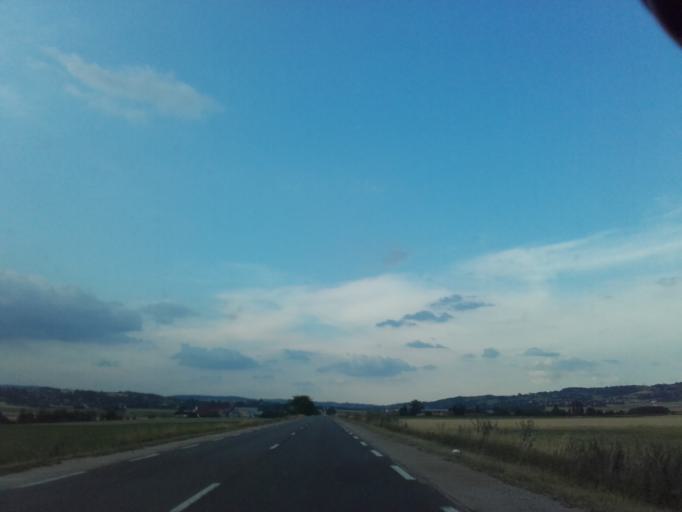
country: FR
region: Rhone-Alpes
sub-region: Departement de l'Isere
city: Auberives-sur-Vareze
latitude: 45.4434
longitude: 4.8210
